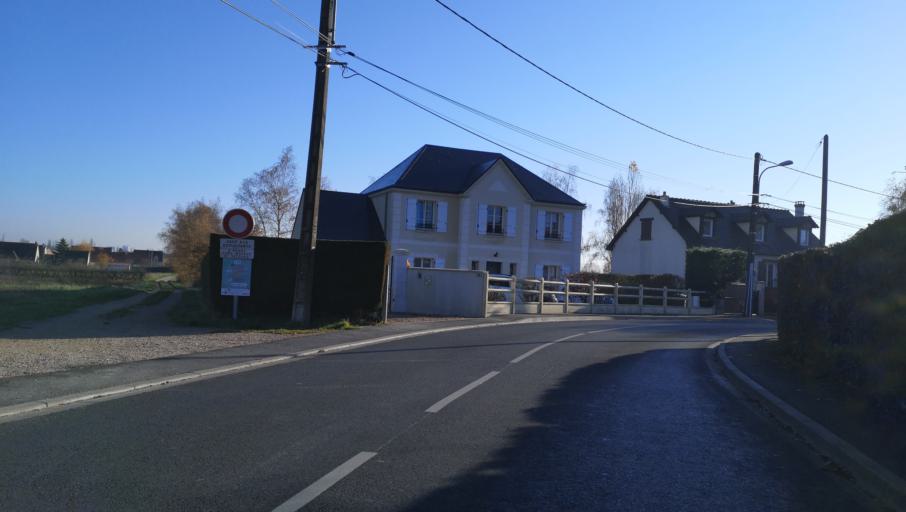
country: FR
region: Centre
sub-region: Departement du Loiret
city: Saint-Jean-de-la-Ruelle
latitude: 47.9313
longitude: 1.8673
